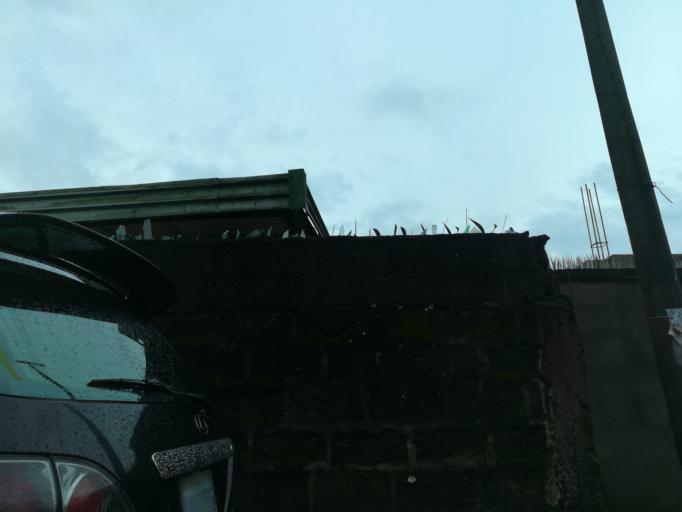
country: NG
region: Rivers
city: Port Harcourt
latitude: 4.8580
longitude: 7.0320
